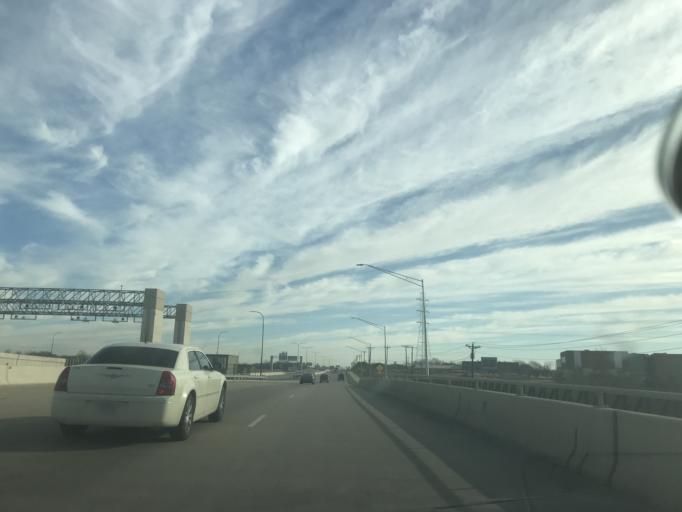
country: US
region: Texas
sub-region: Travis County
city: Manor
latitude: 30.3443
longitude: -97.5789
